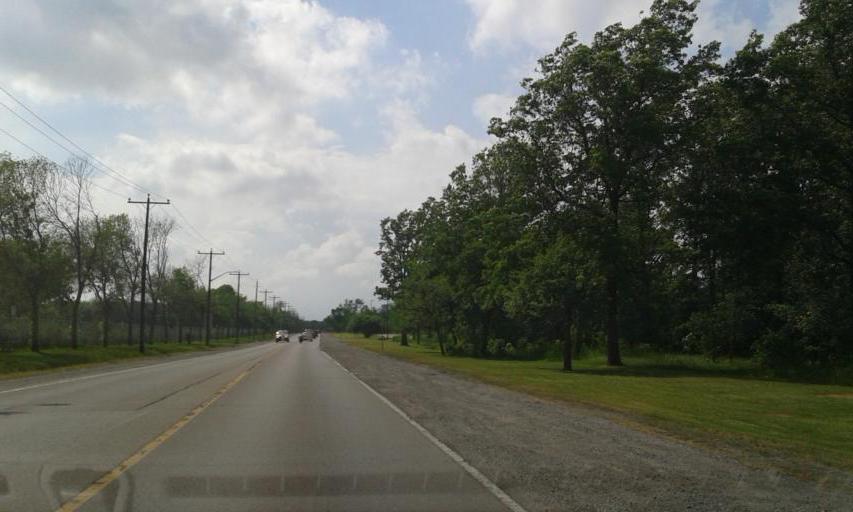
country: US
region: New York
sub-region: Niagara County
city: Niagara Falls
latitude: 43.0637
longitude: -79.0645
